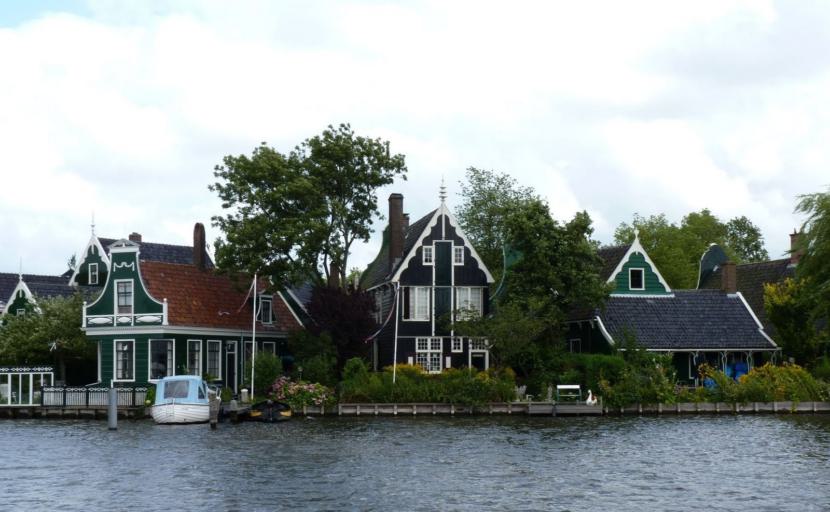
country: NL
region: North Holland
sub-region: Gemeente Zaanstad
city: Zaanstad
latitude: 52.4739
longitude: 4.8157
